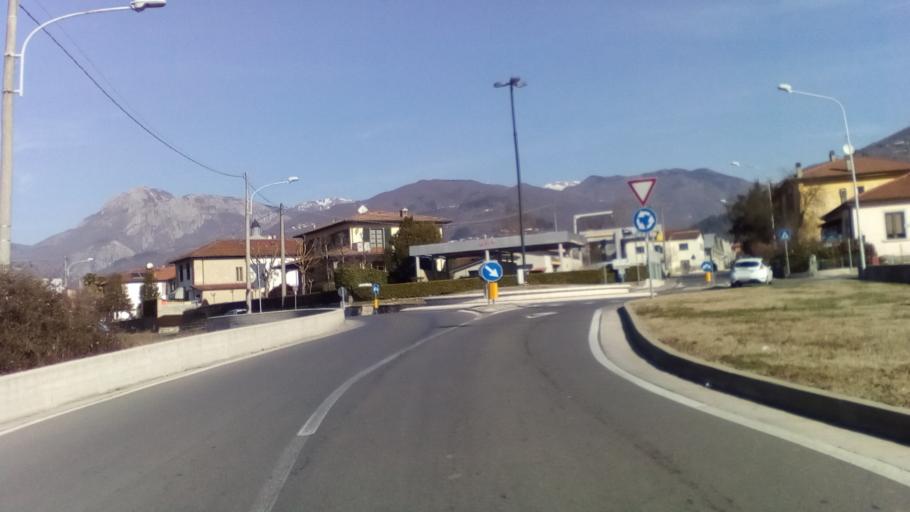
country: IT
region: Tuscany
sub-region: Provincia di Lucca
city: Pieve Fosciana
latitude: 44.1286
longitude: 10.4115
